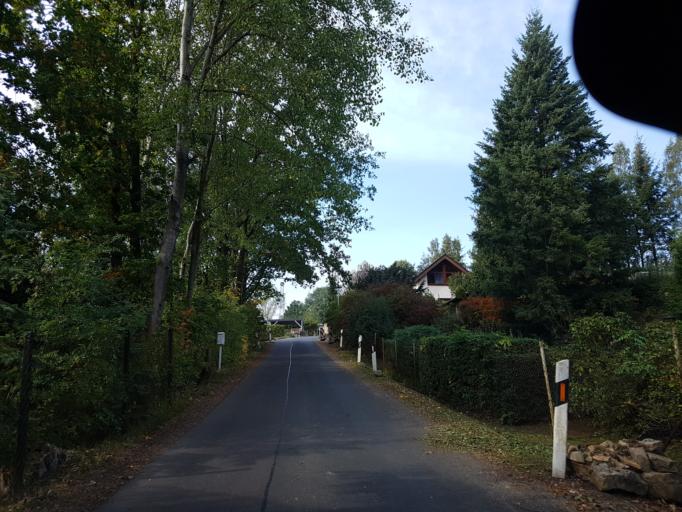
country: DE
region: Saxony
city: Waldheim
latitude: 51.0849
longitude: 13.0051
